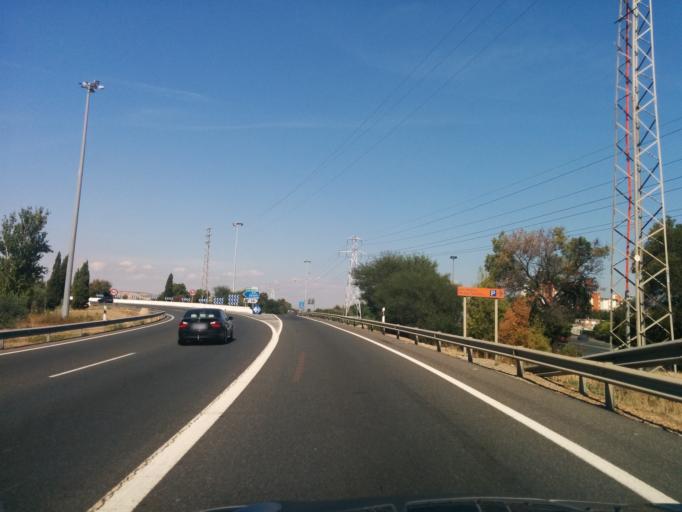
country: ES
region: Andalusia
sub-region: Provincia de Sevilla
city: San Juan de Aznalfarache
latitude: 37.3716
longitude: -6.0139
